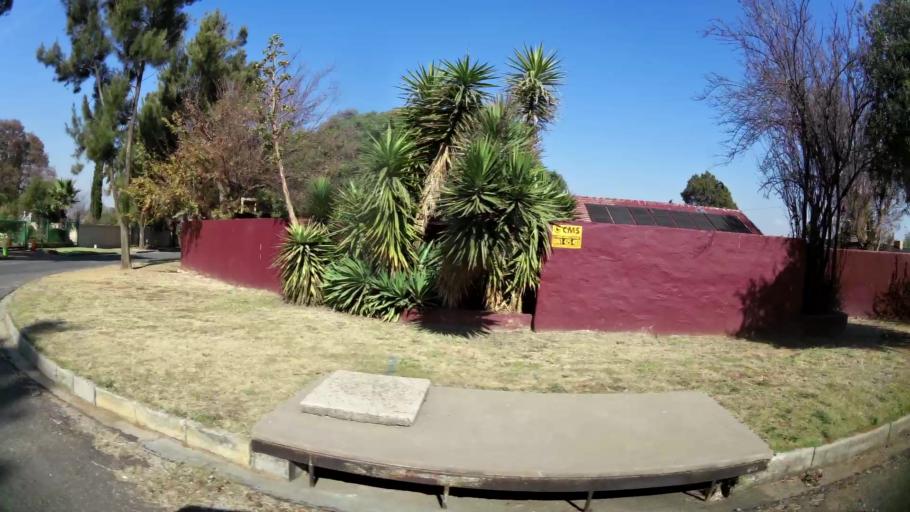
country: ZA
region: Gauteng
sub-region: Ekurhuleni Metropolitan Municipality
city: Boksburg
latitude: -26.1651
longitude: 28.2641
